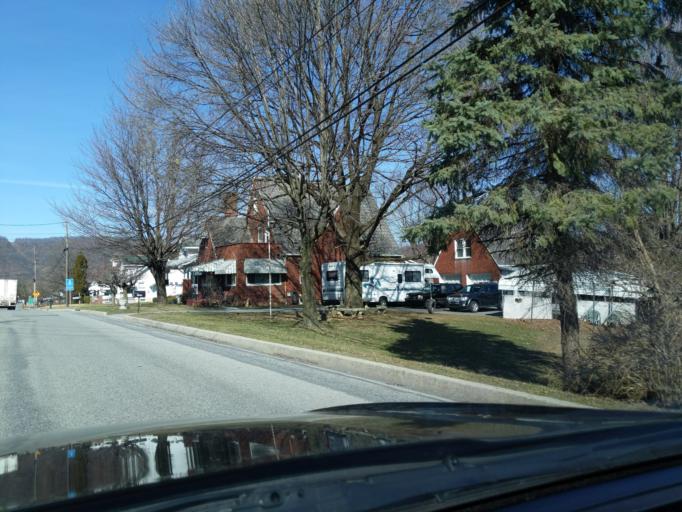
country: US
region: Pennsylvania
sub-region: Blair County
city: Roaring Spring
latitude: 40.3353
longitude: -78.3881
